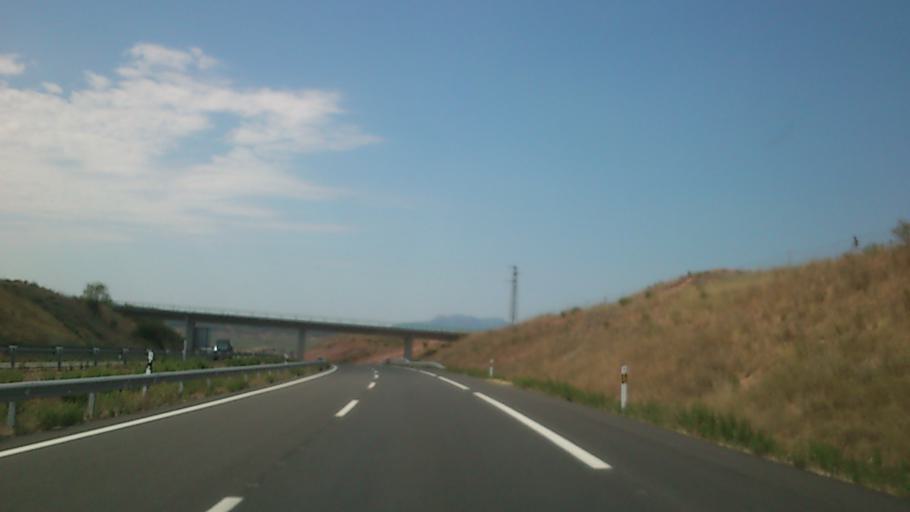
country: ES
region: La Rioja
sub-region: Provincia de La Rioja
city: Fuenmayor
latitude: 42.4548
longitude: -2.5764
